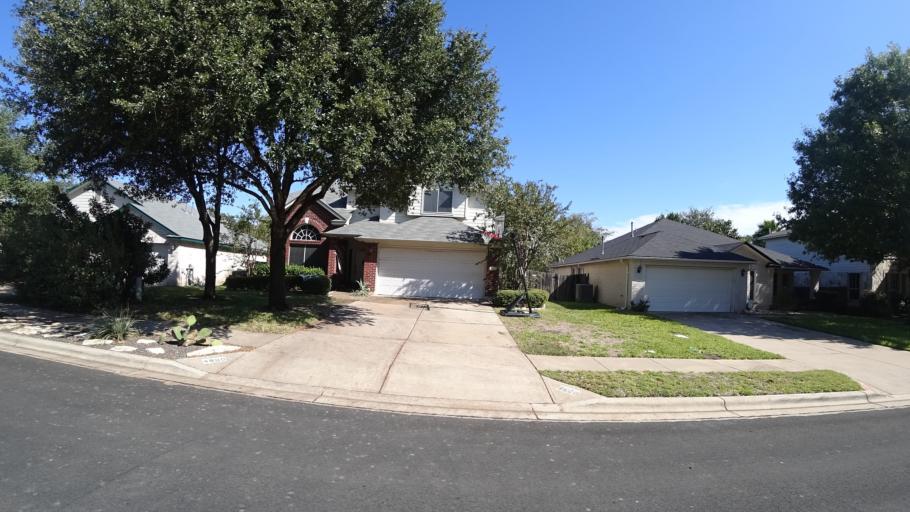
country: US
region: Texas
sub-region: Travis County
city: Shady Hollow
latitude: 30.1961
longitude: -97.8640
